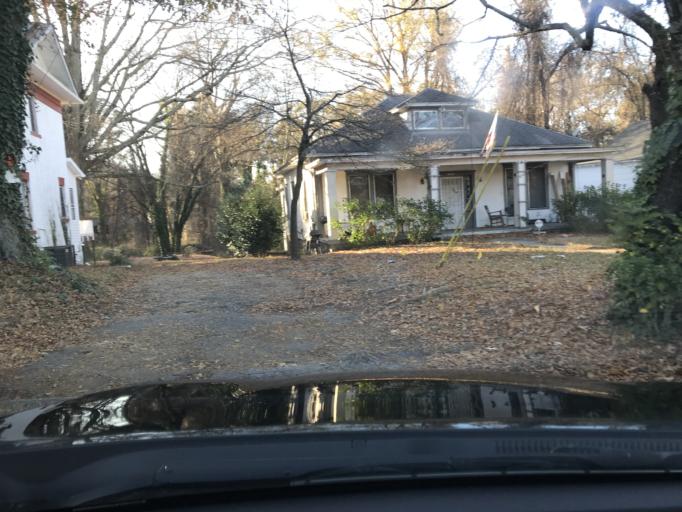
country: US
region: Georgia
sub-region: Fulton County
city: East Point
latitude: 33.7155
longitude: -84.4276
